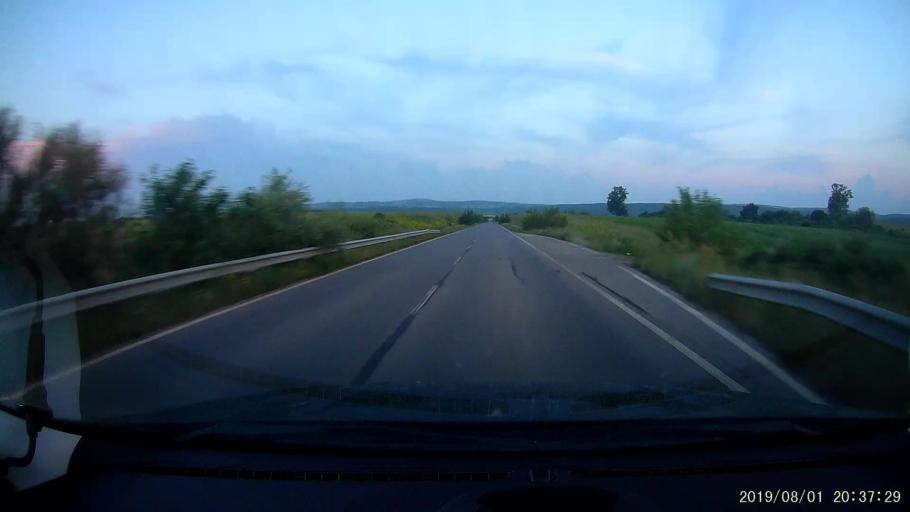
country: BG
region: Yambol
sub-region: Obshtina Elkhovo
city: Elkhovo
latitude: 42.0474
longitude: 26.5941
